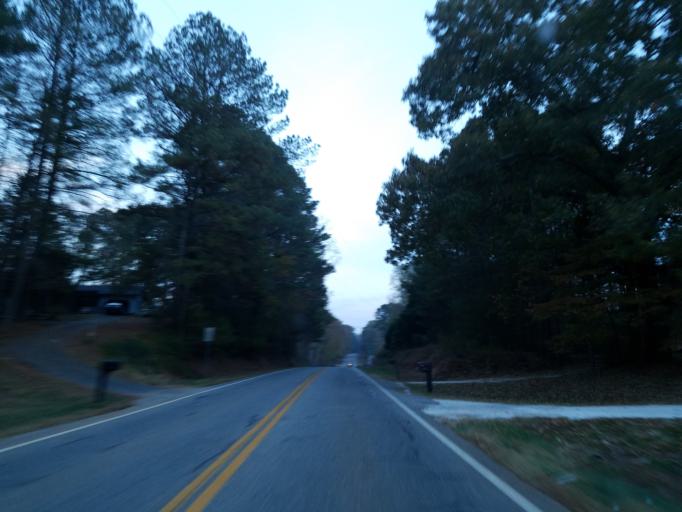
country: US
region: Georgia
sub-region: Gilmer County
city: Ellijay
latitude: 34.5497
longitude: -84.5956
